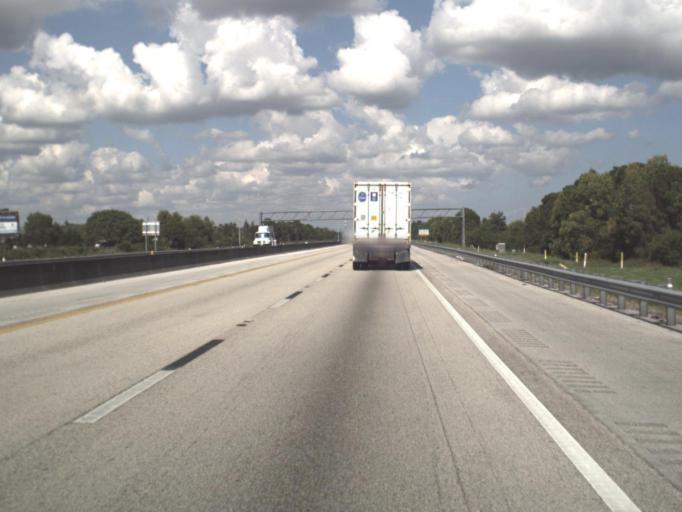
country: US
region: Florida
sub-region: Palm Beach County
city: Limestone Creek
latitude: 26.9146
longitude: -80.1448
